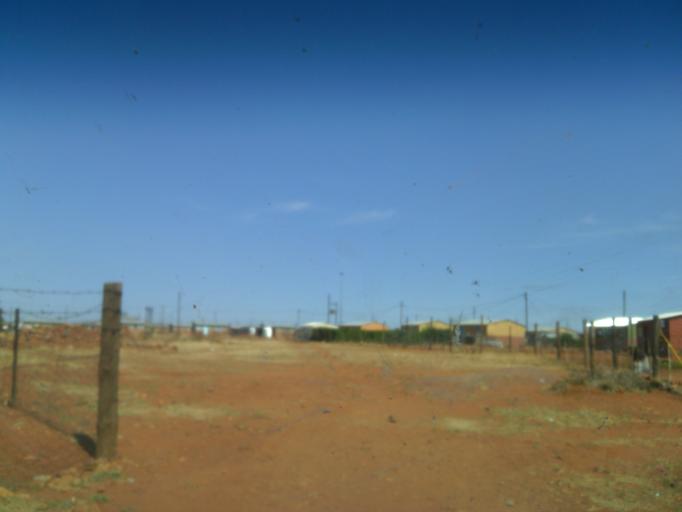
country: ZA
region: Northern Cape
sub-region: Frances Baard District Municipality
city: Barkly West
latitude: -28.5186
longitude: 24.4998
